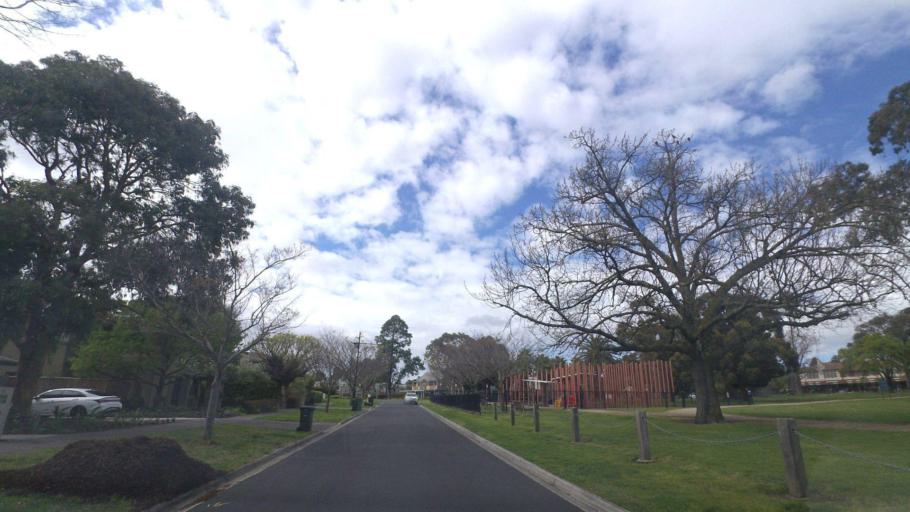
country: AU
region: Victoria
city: Macleod
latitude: -37.7211
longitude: 145.0606
